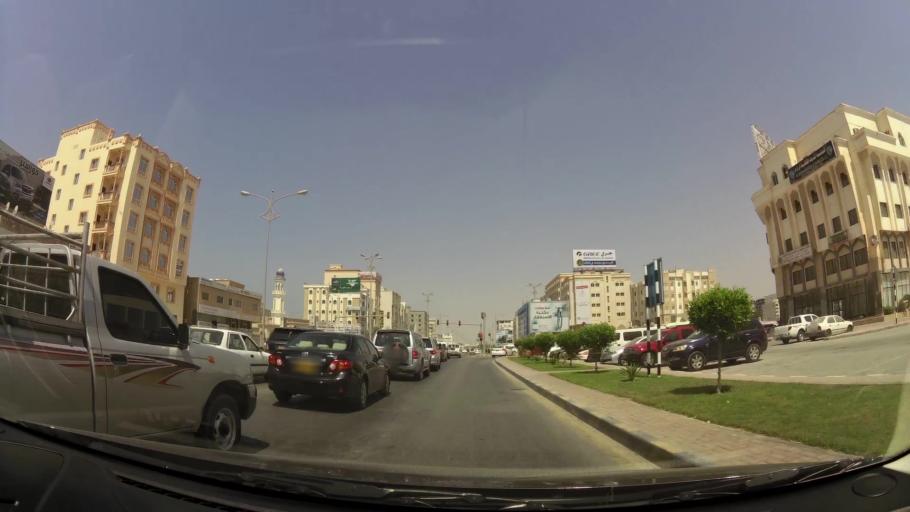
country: OM
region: Zufar
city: Salalah
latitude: 17.0177
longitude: 54.1017
